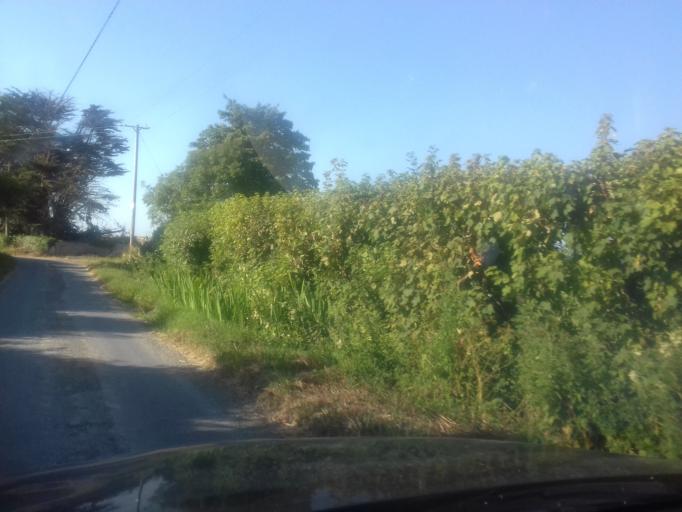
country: IE
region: Leinster
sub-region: Fingal County
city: Blanchardstown
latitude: 53.4401
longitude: -6.3675
